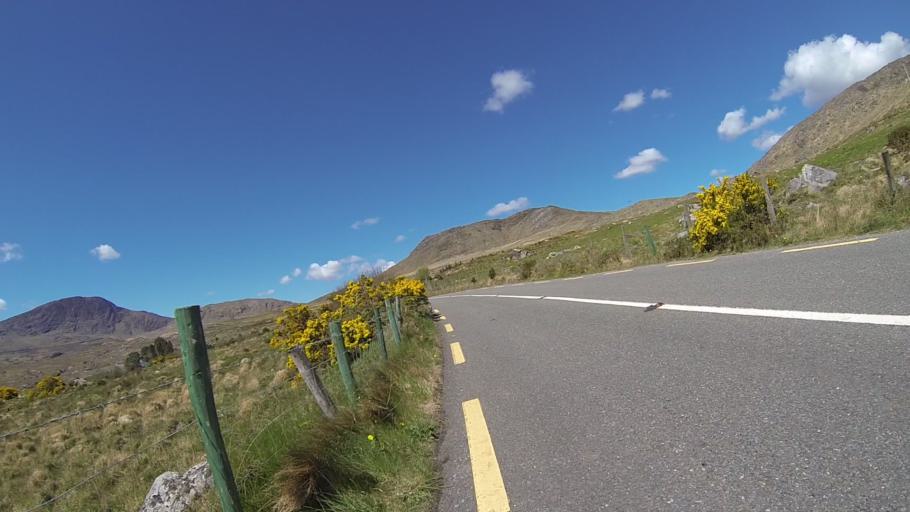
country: IE
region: Munster
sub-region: Ciarrai
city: Kenmare
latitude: 51.9228
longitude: -9.6303
